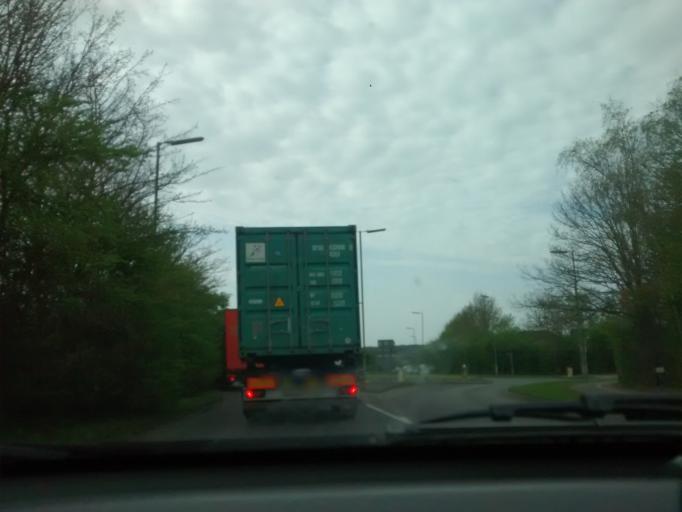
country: GB
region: England
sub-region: Oxfordshire
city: Bicester
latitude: 51.8926
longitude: -1.1287
